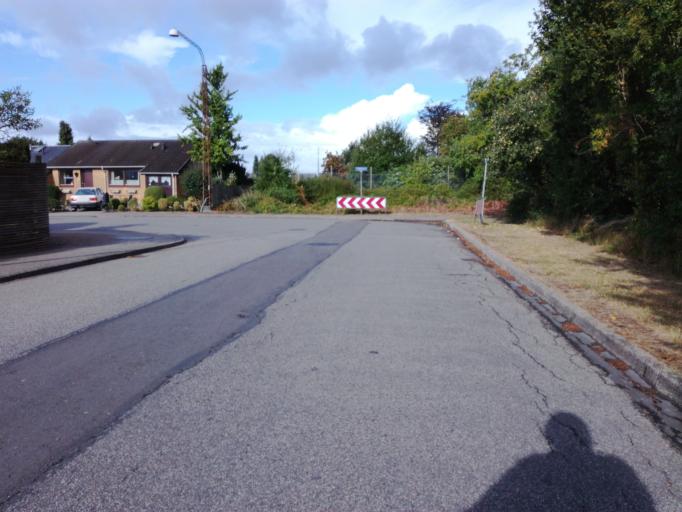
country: DK
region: South Denmark
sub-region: Fredericia Kommune
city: Fredericia
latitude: 55.5830
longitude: 9.7808
